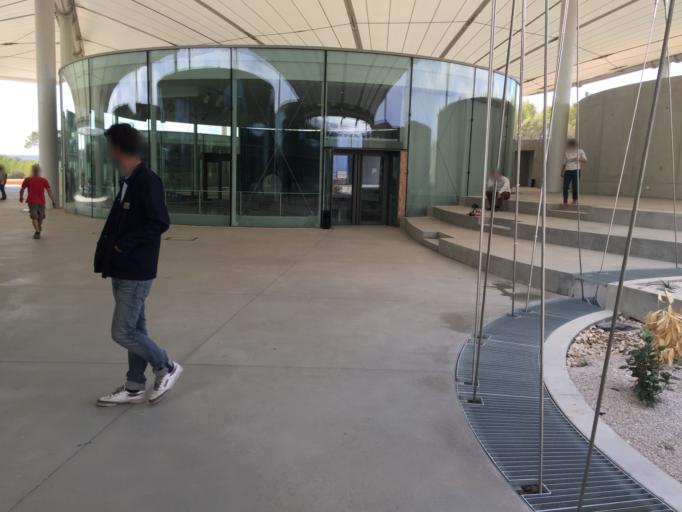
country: FR
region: Provence-Alpes-Cote d'Azur
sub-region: Departement des Bouches-du-Rhone
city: Ventabren
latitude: 43.4984
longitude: 5.3420
